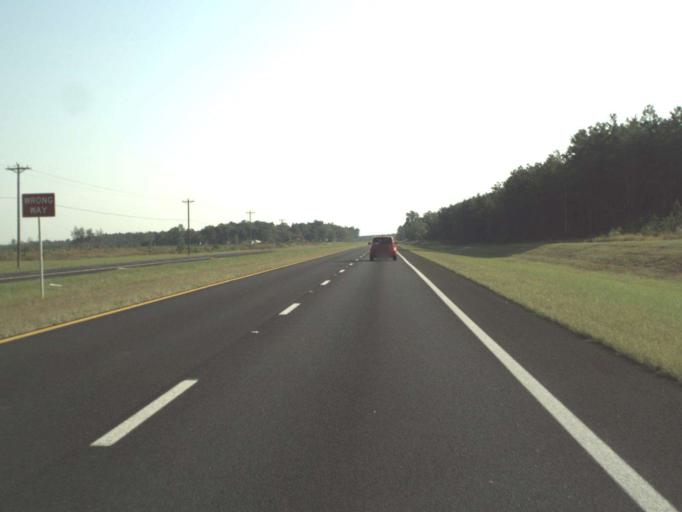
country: US
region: Florida
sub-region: Bay County
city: Laguna Beach
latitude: 30.4632
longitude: -85.8632
